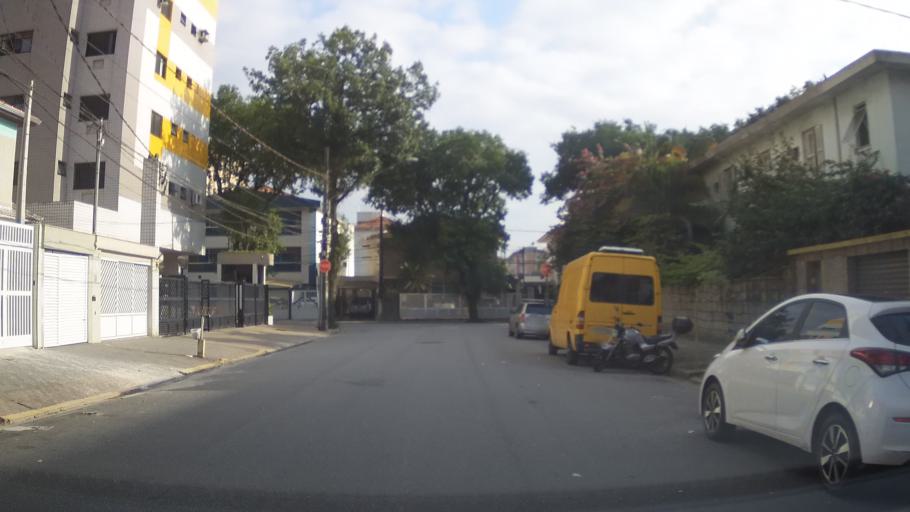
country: BR
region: Sao Paulo
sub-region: Santos
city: Santos
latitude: -23.9585
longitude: -46.3248
